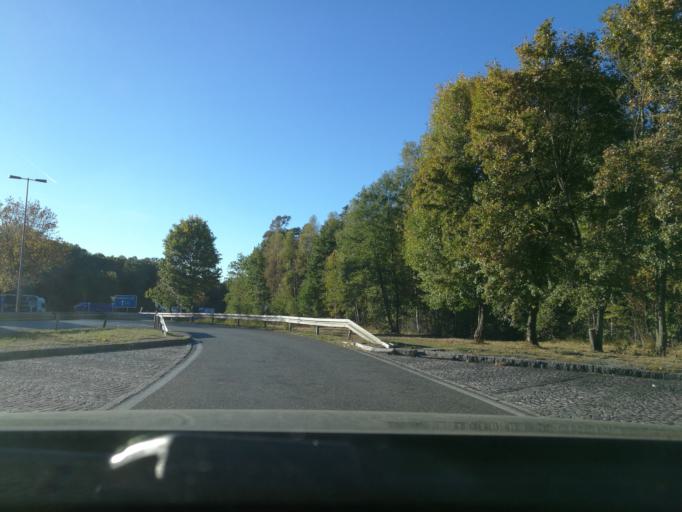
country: DE
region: Bavaria
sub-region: Regierungsbezirk Mittelfranken
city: Wetzendorf
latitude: 49.5271
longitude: 11.0672
